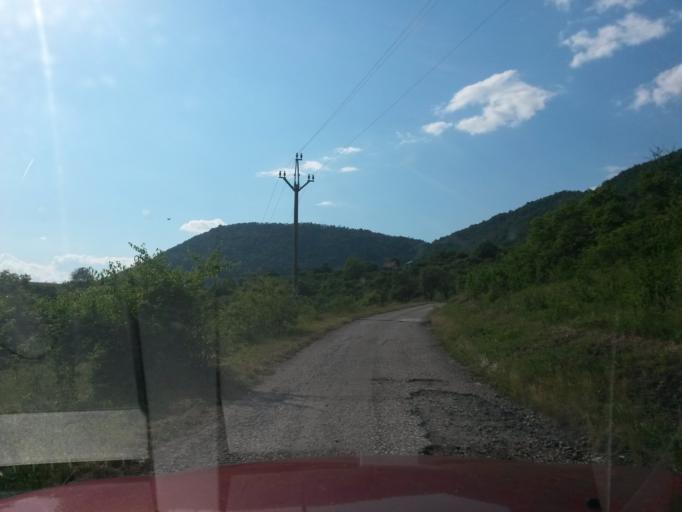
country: SK
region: Kosicky
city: Roznava
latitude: 48.5966
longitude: 20.6545
